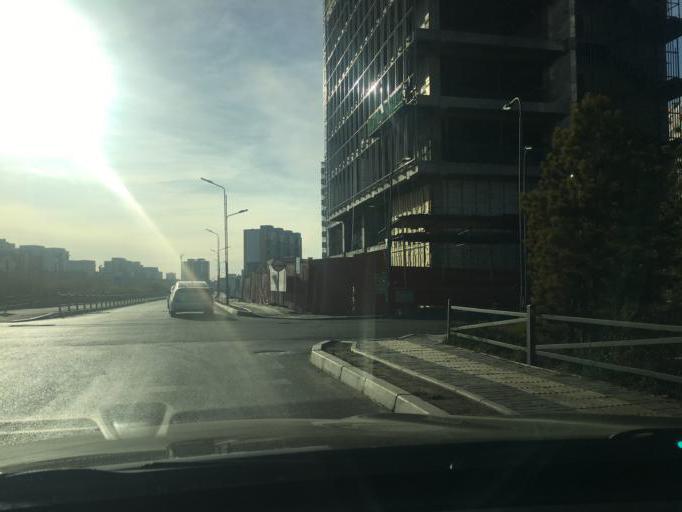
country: MN
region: Ulaanbaatar
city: Ulaanbaatar
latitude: 47.9055
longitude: 106.9069
